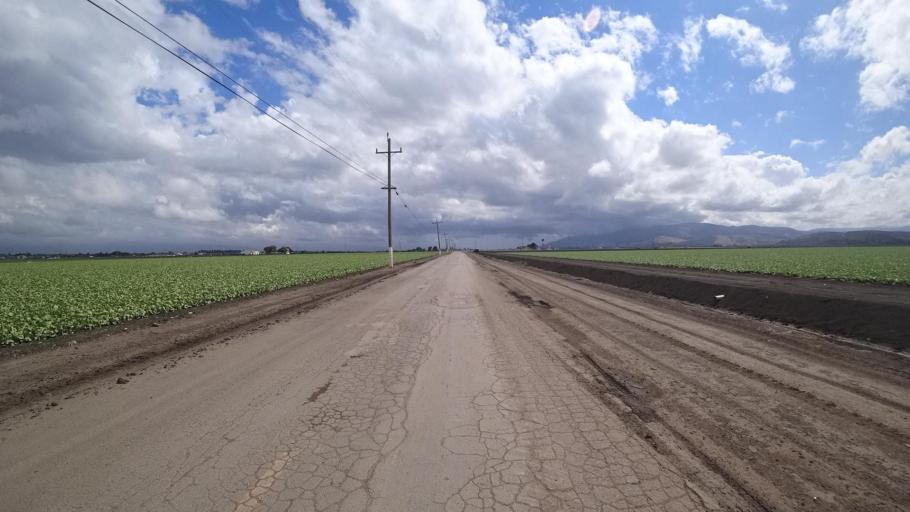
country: US
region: California
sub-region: Monterey County
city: Boronda
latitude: 36.6606
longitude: -121.6953
